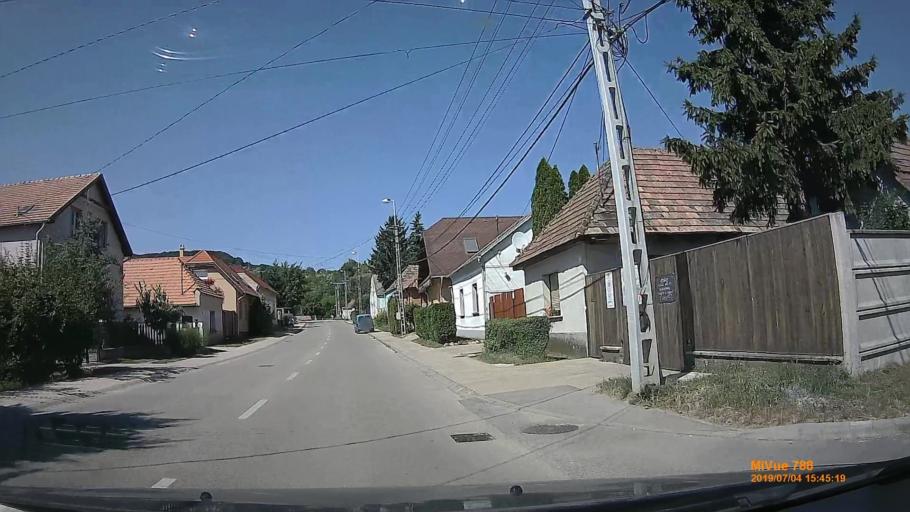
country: HU
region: Komarom-Esztergom
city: Tatabanya
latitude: 47.5712
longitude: 18.4156
